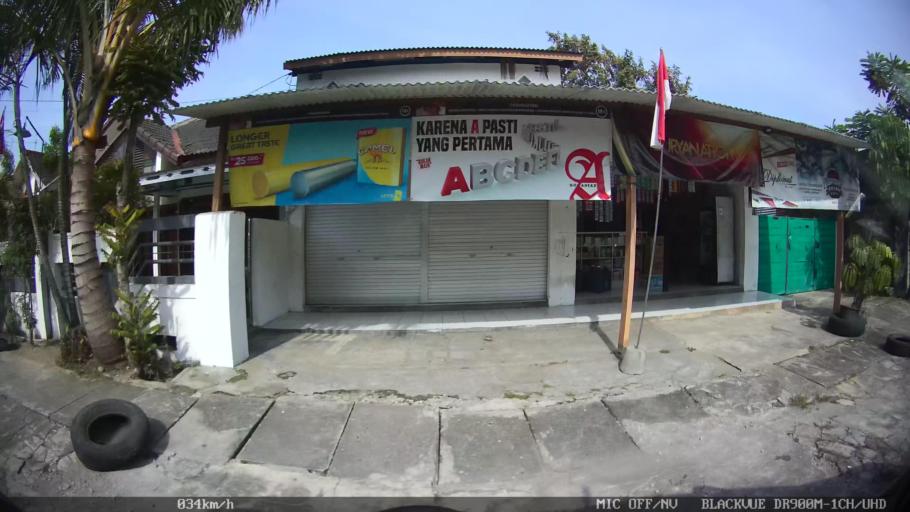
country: ID
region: Daerah Istimewa Yogyakarta
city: Depok
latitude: -7.7668
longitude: 110.4250
